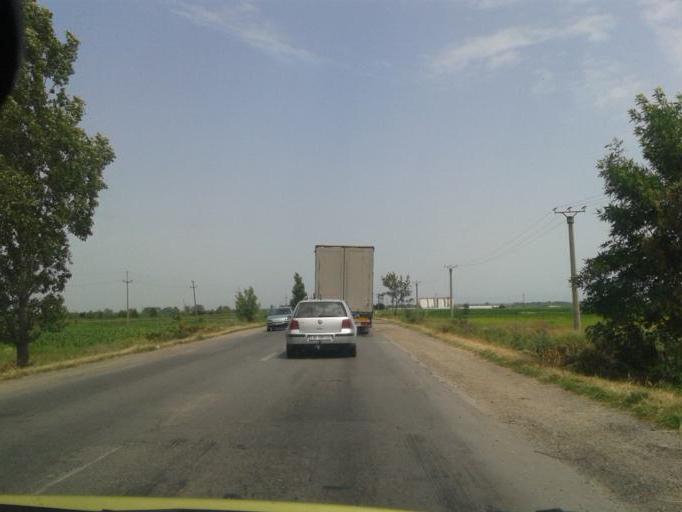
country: RO
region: Dambovita
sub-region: Oras Gaesti
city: Gaesti
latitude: 44.6892
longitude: 25.3132
